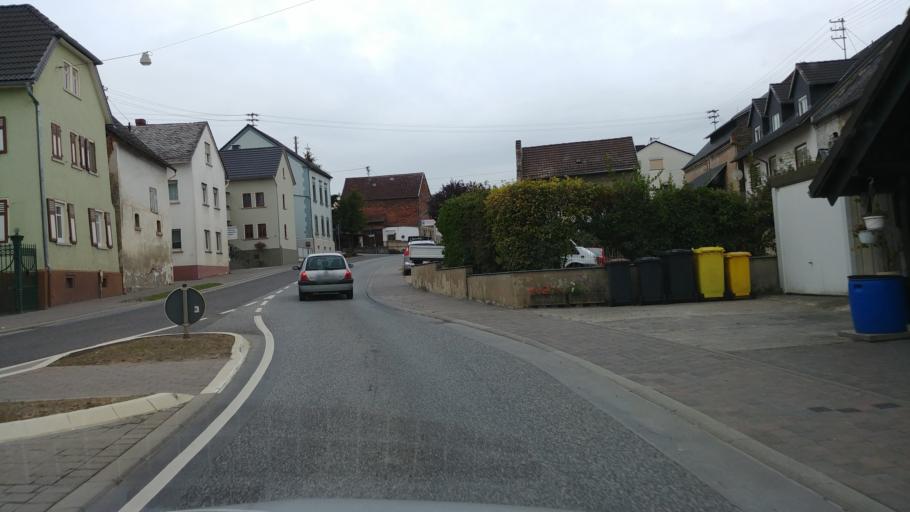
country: DE
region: Rheinland-Pfalz
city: Niederneisen
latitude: 50.3355
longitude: 8.0549
